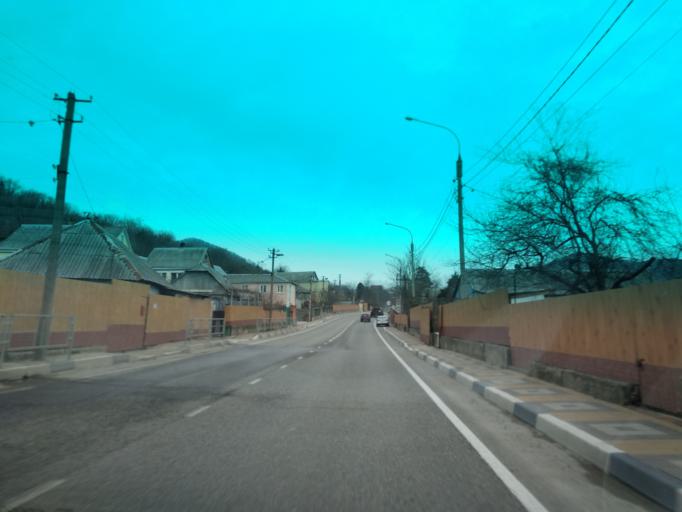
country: RU
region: Krasnodarskiy
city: Ol'ginka
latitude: 44.2093
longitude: 38.8920
